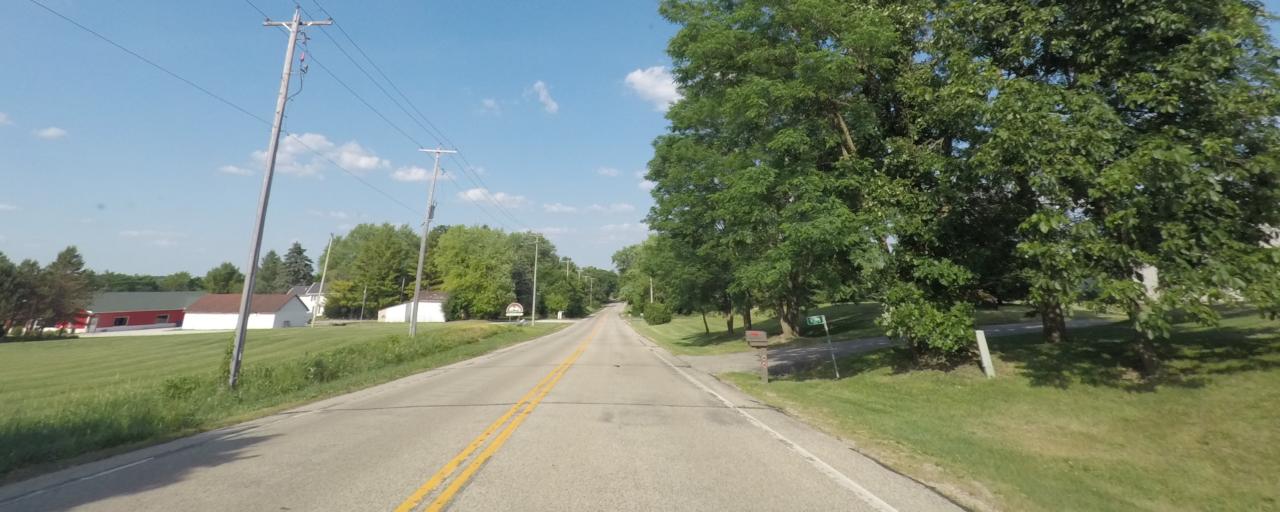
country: US
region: Wisconsin
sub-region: Walworth County
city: Potter Lake
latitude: 42.8053
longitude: -88.3638
